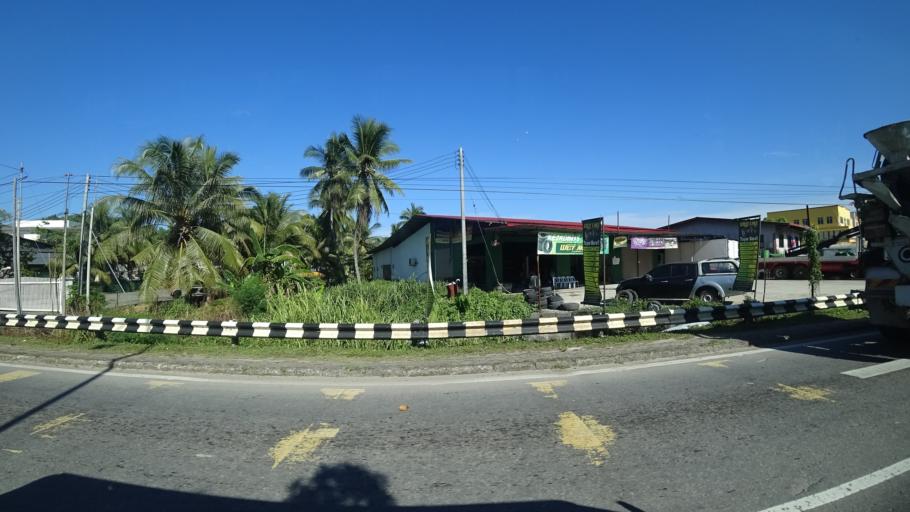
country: MY
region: Sabah
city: Kota Kinabalu
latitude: 6.1460
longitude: 116.2216
